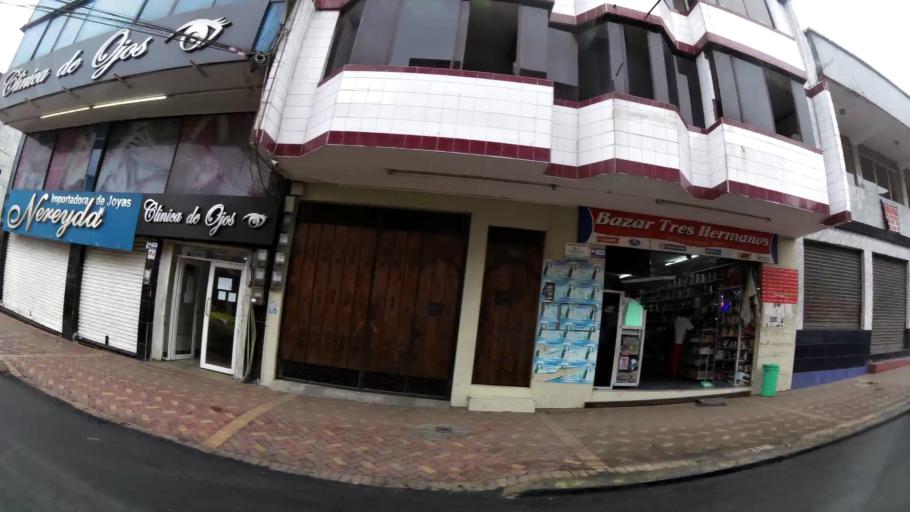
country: EC
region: Santo Domingo de los Tsachilas
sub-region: Canton Santo Domingo de los Colorados
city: Santo Domingo de los Colorados
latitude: -0.2549
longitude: -79.1739
